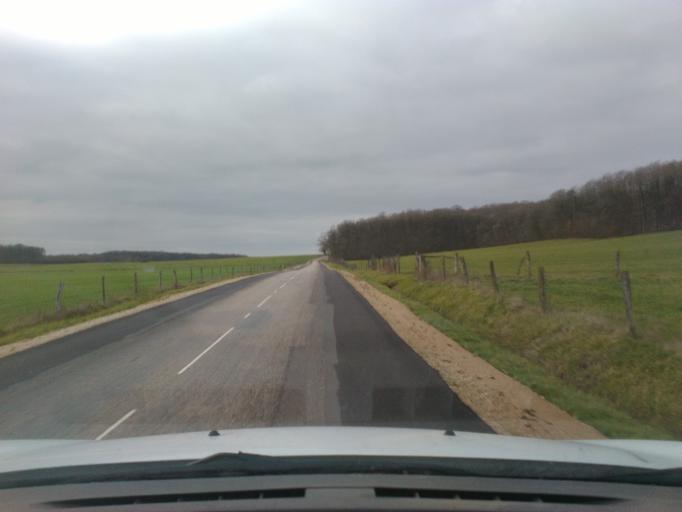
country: FR
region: Lorraine
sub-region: Departement des Vosges
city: Mirecourt
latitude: 48.3372
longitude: 6.0064
